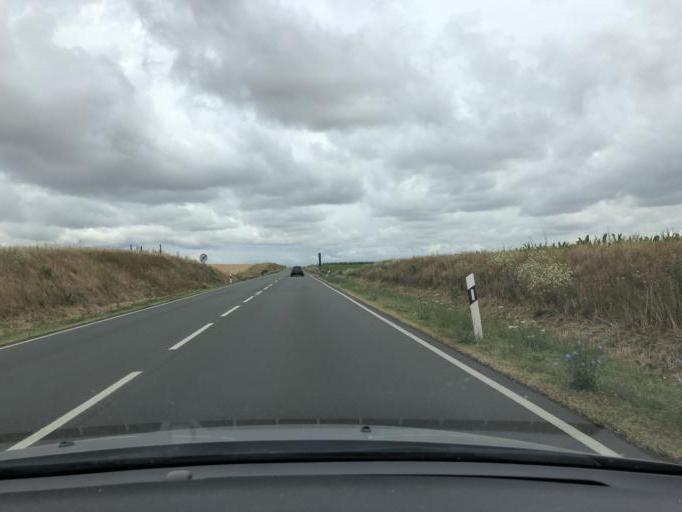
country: DE
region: Saxony-Anhalt
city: Erdeborn
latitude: 51.4907
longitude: 11.6617
